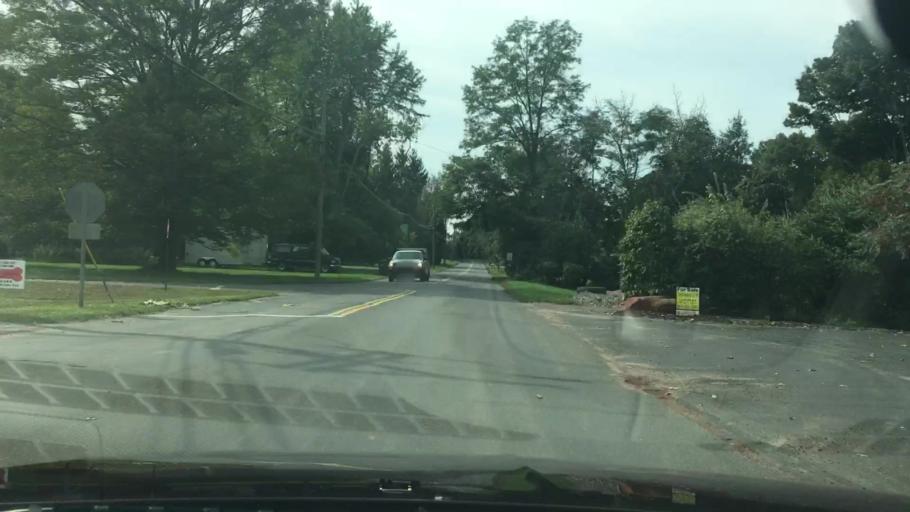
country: US
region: Connecticut
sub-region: Hartford County
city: Broad Brook
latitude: 41.8899
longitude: -72.5366
